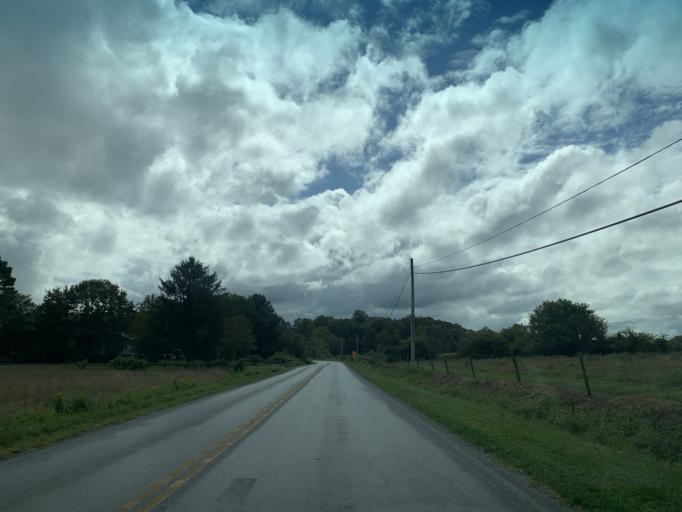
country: US
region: Maryland
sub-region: Caroline County
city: Denton
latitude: 38.9054
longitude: -75.8391
